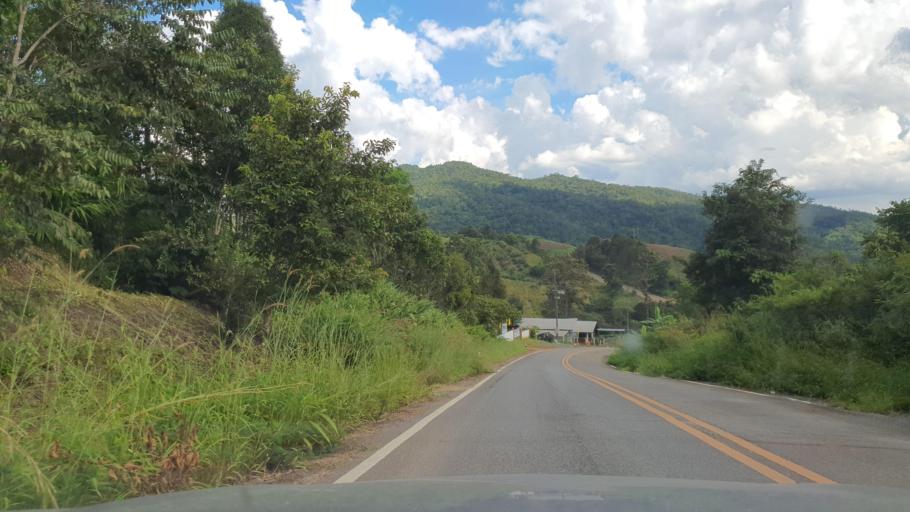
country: TH
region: Chiang Rai
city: Wiang Pa Pao
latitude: 19.3111
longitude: 99.4086
